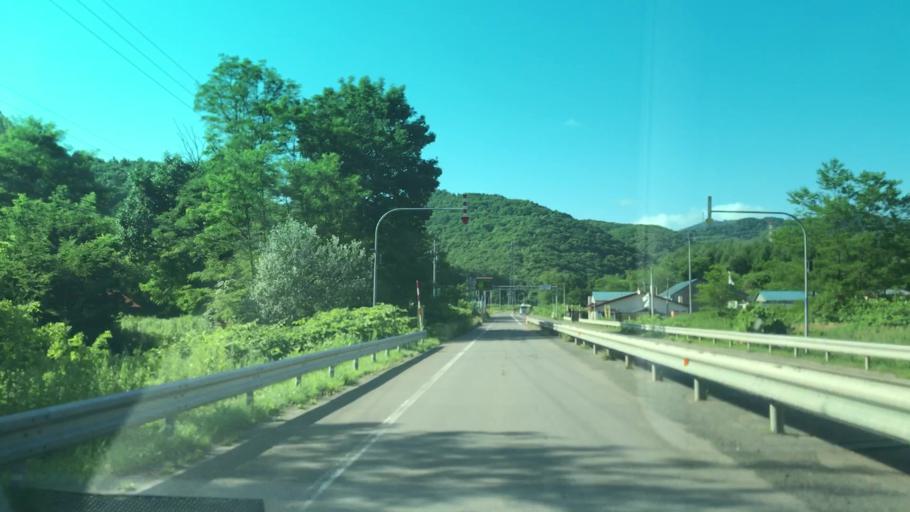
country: JP
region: Hokkaido
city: Iwanai
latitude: 43.0044
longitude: 140.6673
